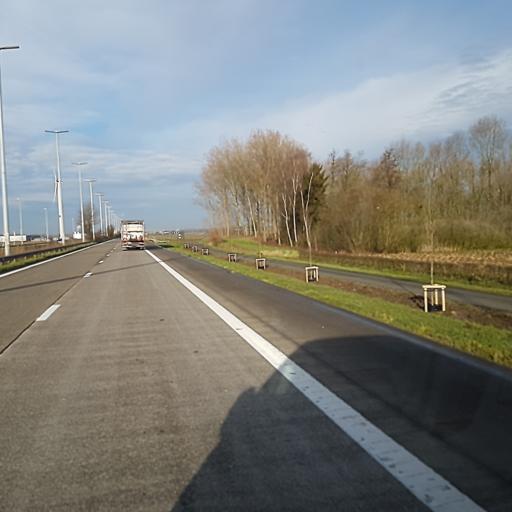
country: BE
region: Flanders
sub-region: Provincie Oost-Vlaanderen
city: Sint-Gillis-Waas
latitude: 51.2326
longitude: 4.1333
